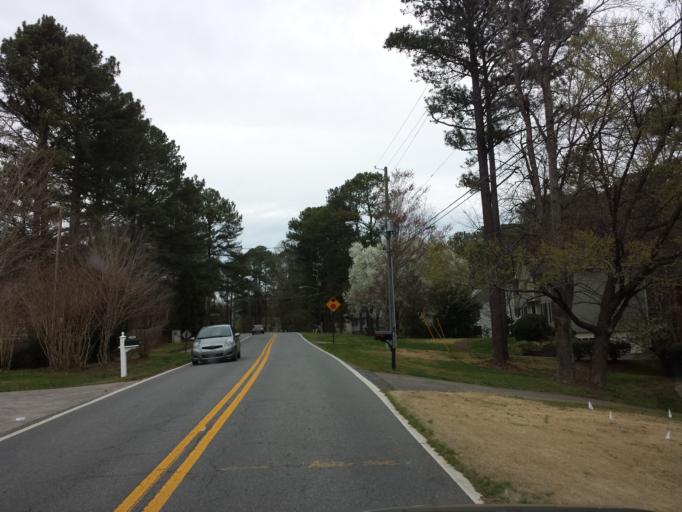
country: US
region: Georgia
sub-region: Cherokee County
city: Woodstock
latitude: 34.0285
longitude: -84.5101
